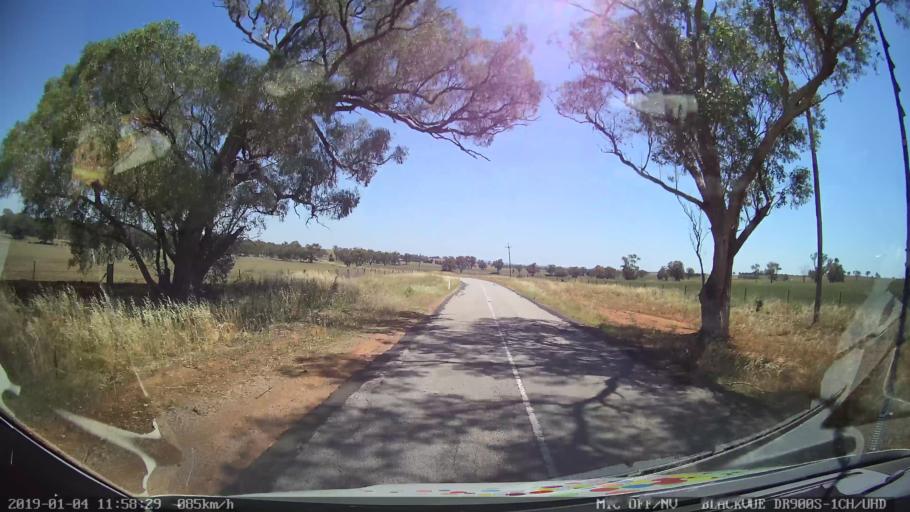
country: AU
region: New South Wales
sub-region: Cabonne
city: Molong
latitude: -32.8239
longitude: 148.7013
